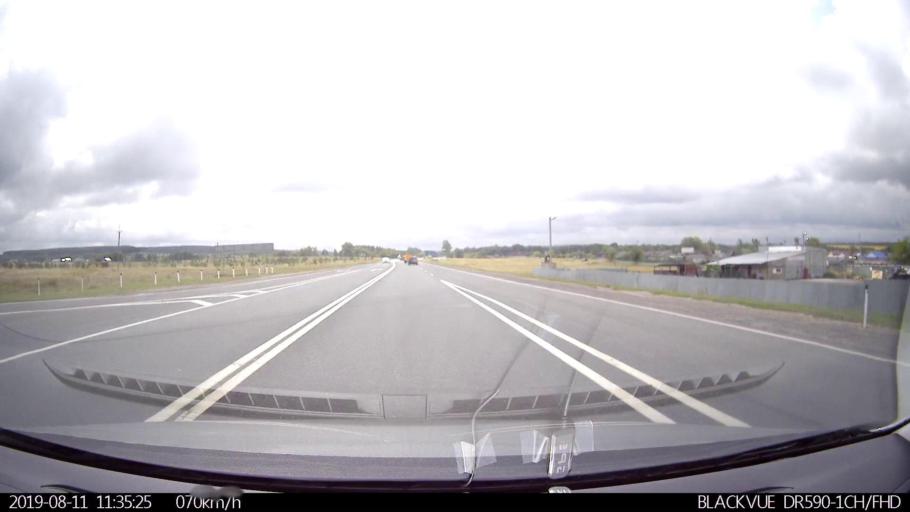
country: RU
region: Ulyanovsk
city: Silikatnyy
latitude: 54.0064
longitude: 48.2195
